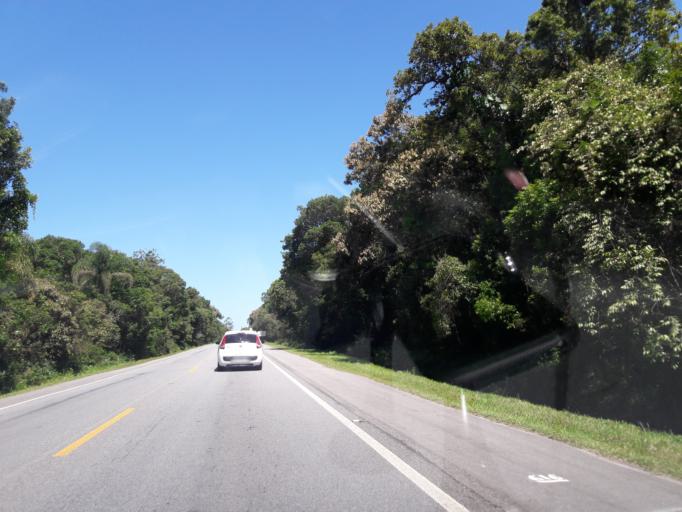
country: BR
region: Parana
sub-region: Pontal Do Parana
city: Pontal do Parana
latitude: -25.6581
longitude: -48.5227
